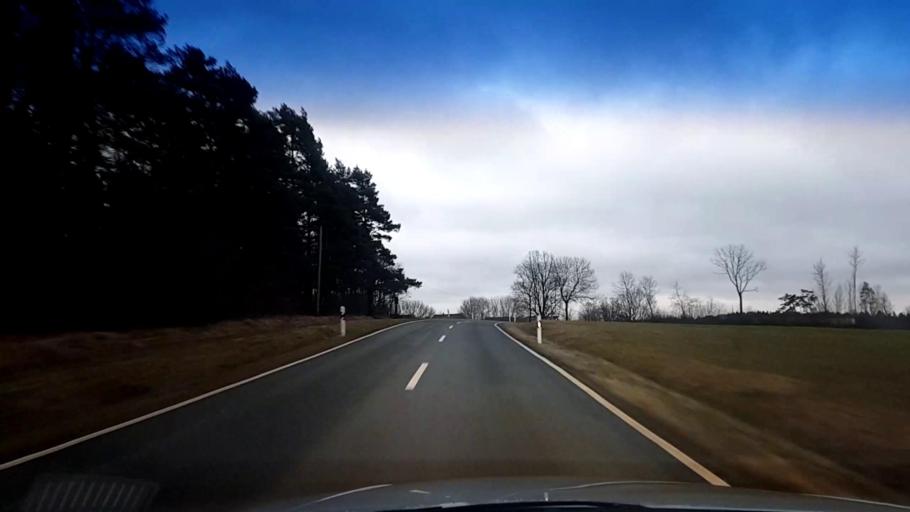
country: DE
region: Bavaria
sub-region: Upper Franconia
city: Wattendorf
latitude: 50.0460
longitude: 11.0622
